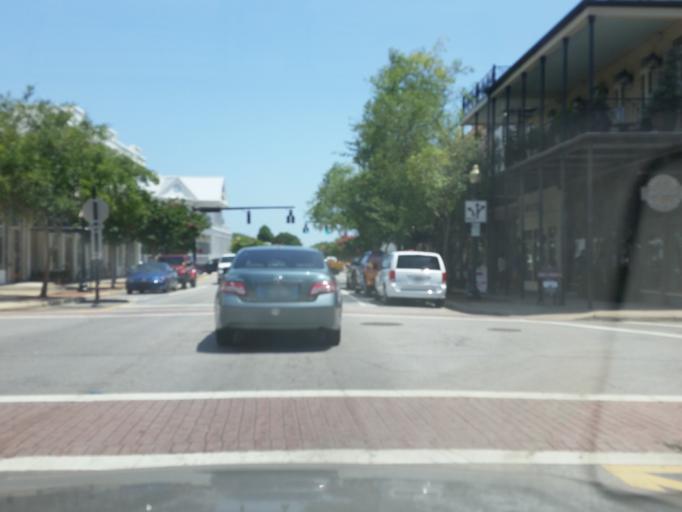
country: US
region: Florida
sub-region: Escambia County
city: Pensacola
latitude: 30.4083
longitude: -87.2144
